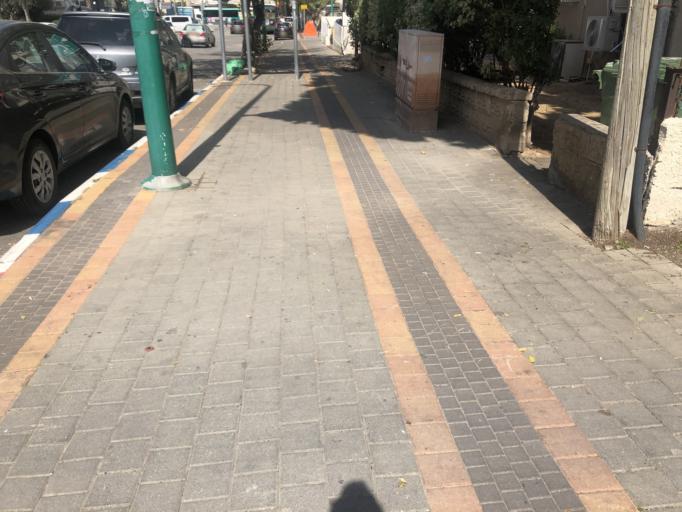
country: IL
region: Haifa
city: Hadera
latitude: 32.4391
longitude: 34.9178
